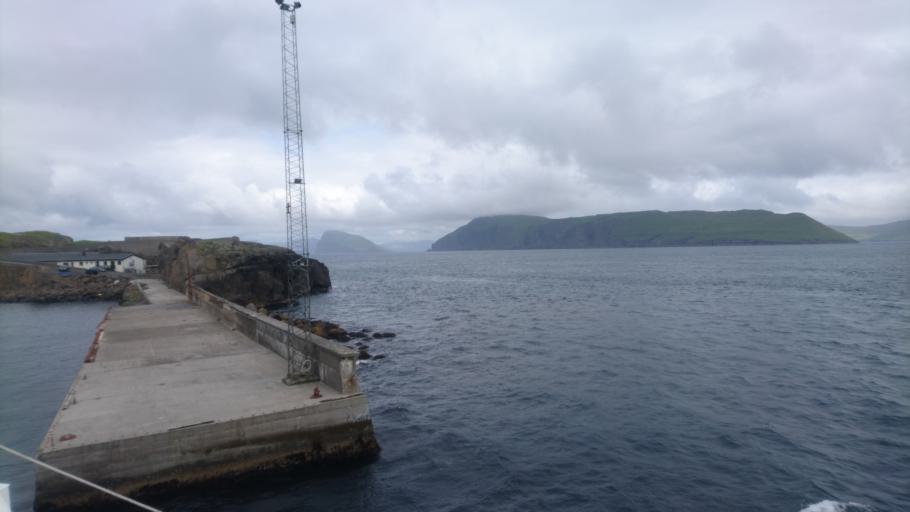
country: FO
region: Sandoy
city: Sandur
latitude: 61.9047
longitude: -6.8785
